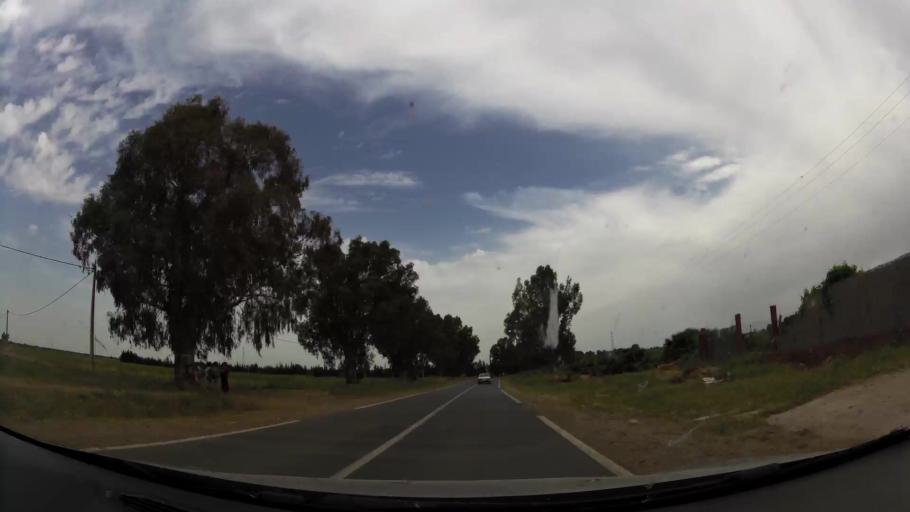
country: MA
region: Rabat-Sale-Zemmour-Zaer
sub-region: Khemisset
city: Tiflet
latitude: 33.8633
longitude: -6.2717
